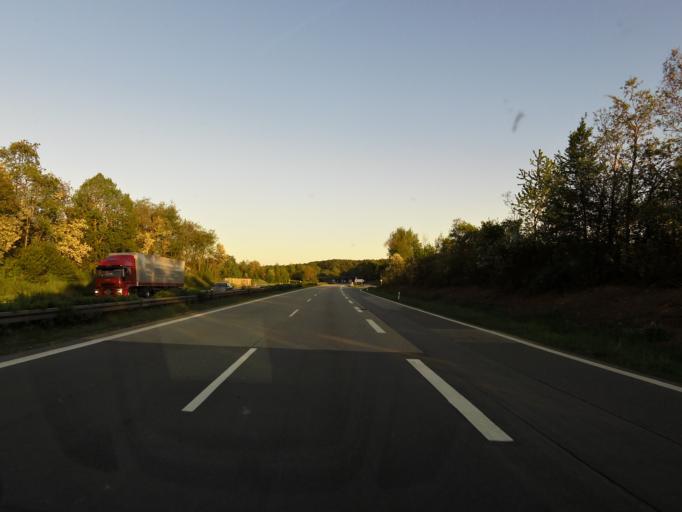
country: DE
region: Bavaria
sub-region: Lower Bavaria
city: Iggensbach
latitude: 48.7313
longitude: 13.1320
